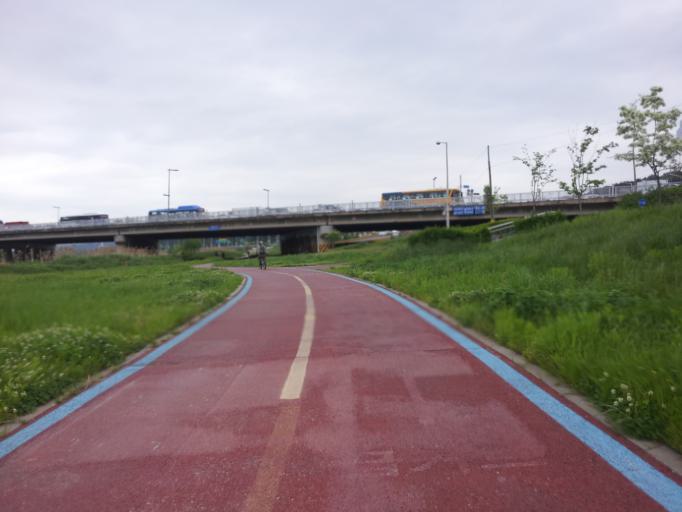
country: KR
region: Daejeon
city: Daejeon
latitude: 36.3559
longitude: 127.4050
